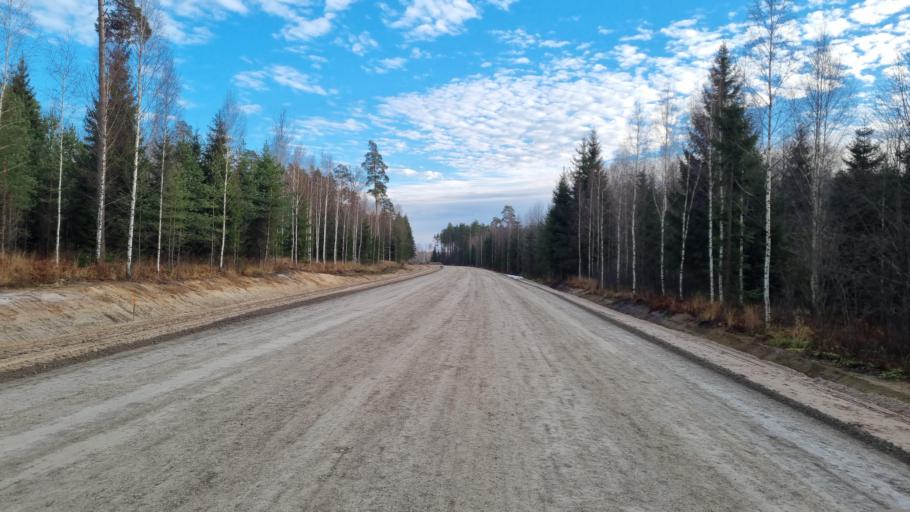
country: LV
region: Kekava
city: Kekava
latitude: 56.7910
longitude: 24.2153
